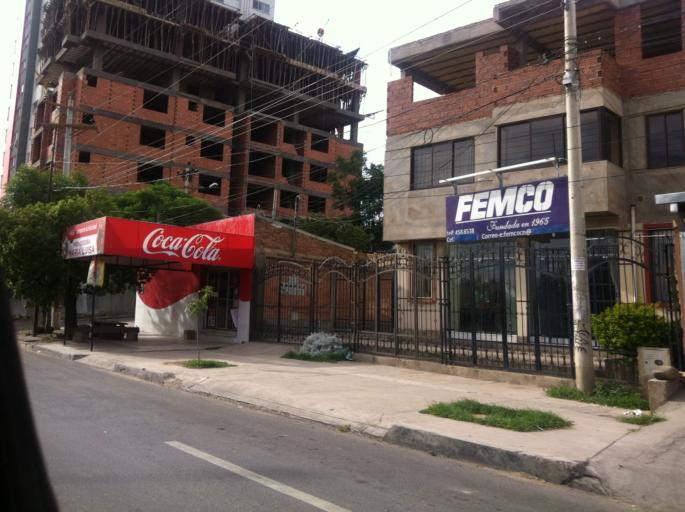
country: BO
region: Cochabamba
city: Cochabamba
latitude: -17.3740
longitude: -66.1373
